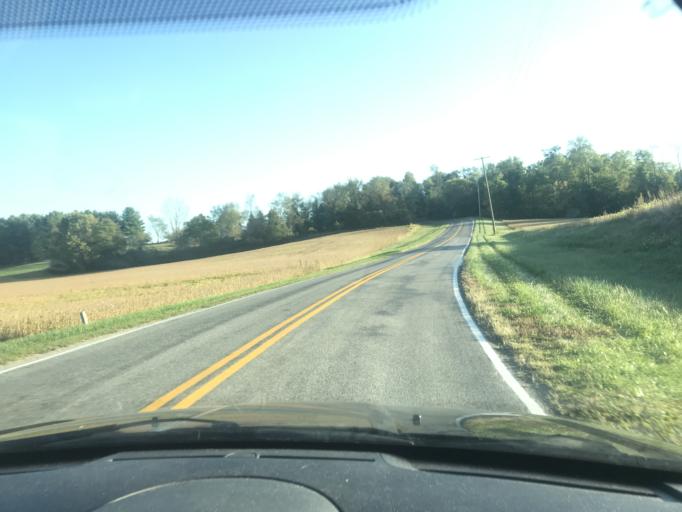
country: US
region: Ohio
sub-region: Logan County
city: De Graff
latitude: 40.2423
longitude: -83.8639
